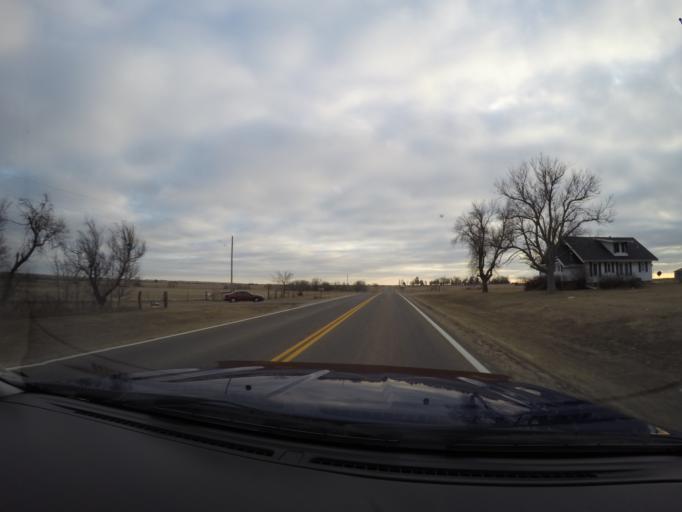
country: US
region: Kansas
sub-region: Morris County
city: Council Grove
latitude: 38.7700
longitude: -96.5012
